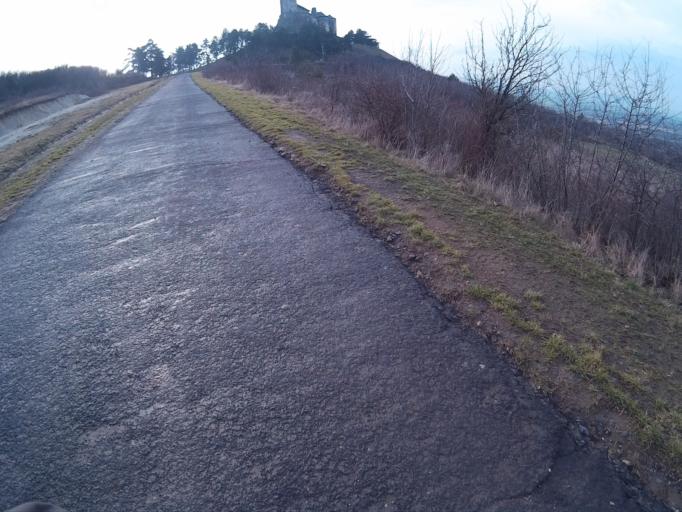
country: HU
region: Borsod-Abauj-Zemplen
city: Abaujszanto
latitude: 48.3468
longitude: 21.2310
